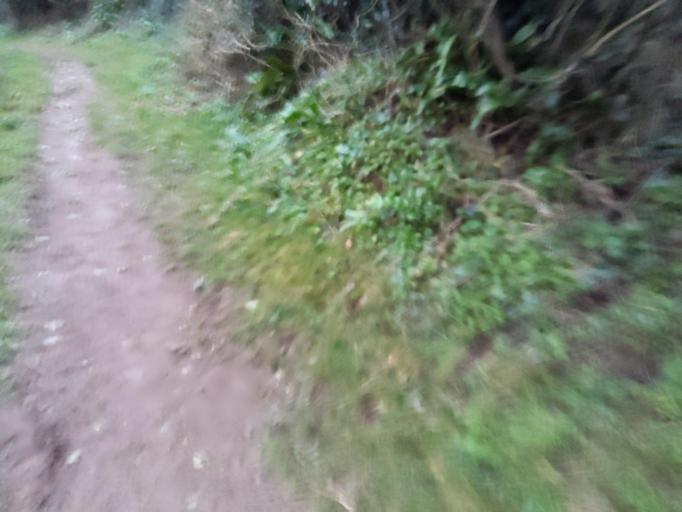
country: GB
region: England
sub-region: Cornwall
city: Millbrook
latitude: 50.3199
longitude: -4.2224
